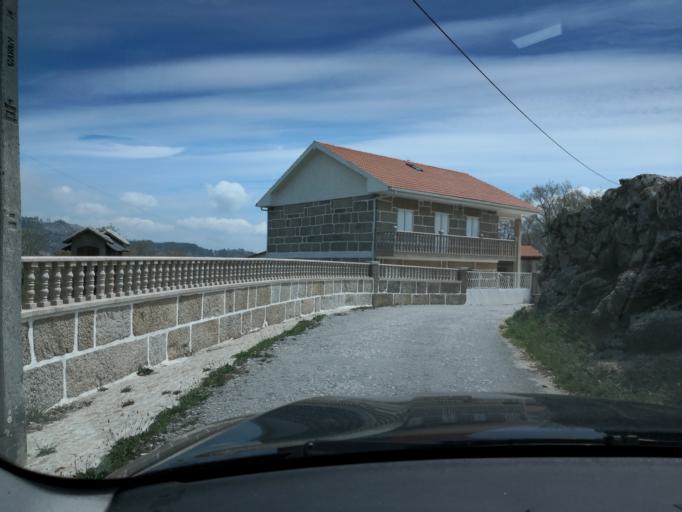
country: PT
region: Vila Real
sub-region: Vila Real
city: Vila Real
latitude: 41.3344
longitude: -7.8081
